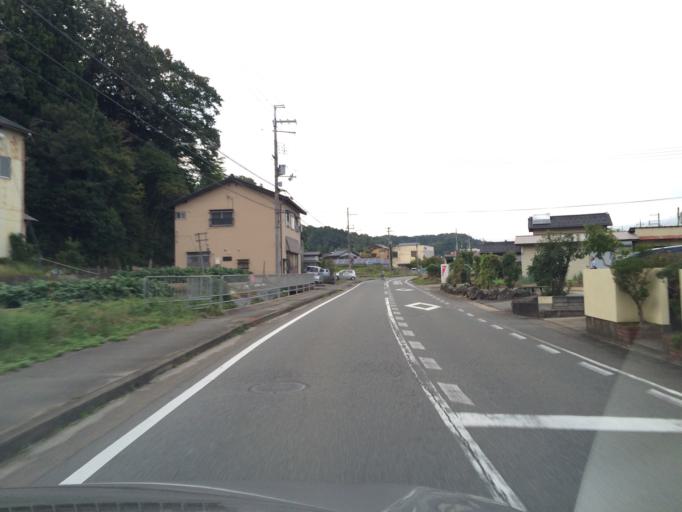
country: JP
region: Hyogo
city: Toyooka
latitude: 35.5236
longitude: 134.8181
